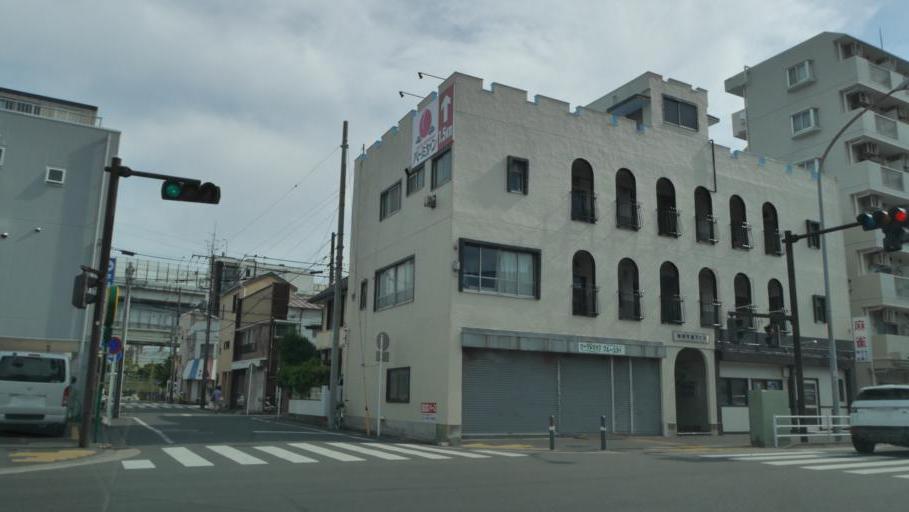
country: JP
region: Kanagawa
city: Yokohama
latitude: 35.4185
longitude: 139.6407
